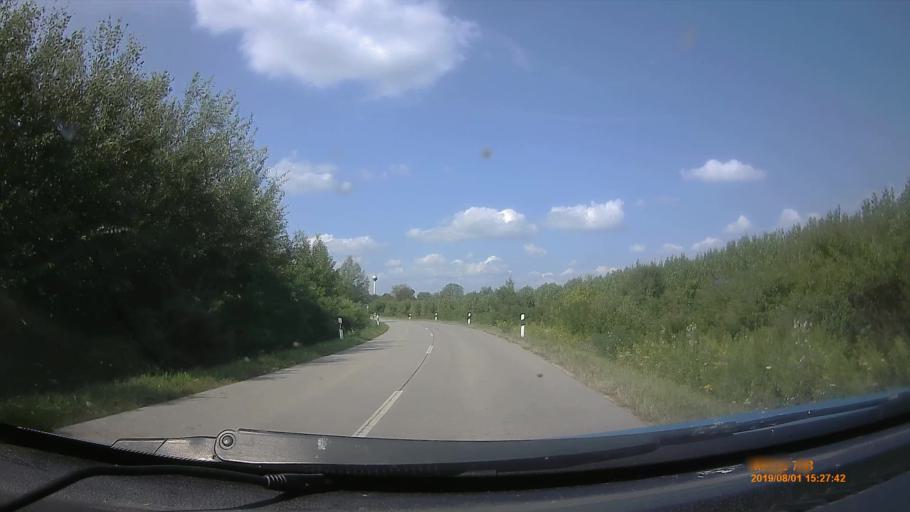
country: HU
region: Baranya
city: Sellye
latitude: 45.9087
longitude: 17.8639
